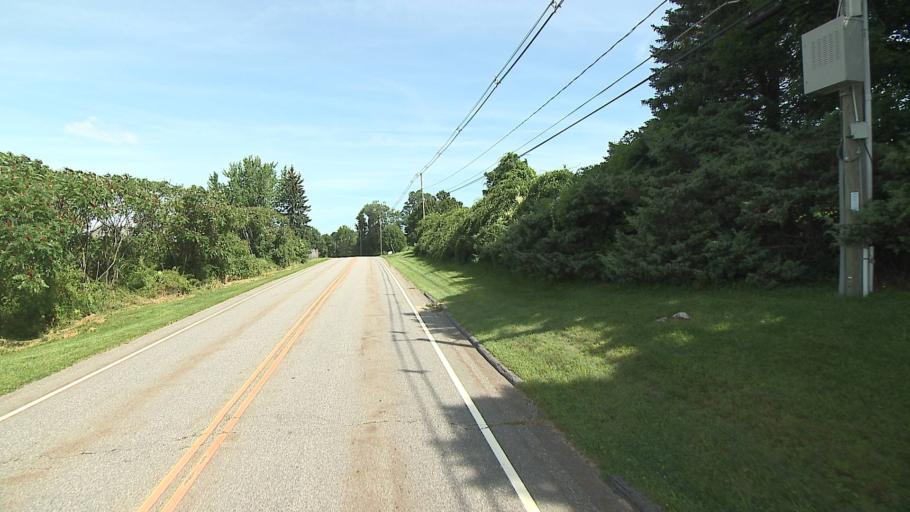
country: US
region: Connecticut
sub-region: Litchfield County
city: Bethlehem Village
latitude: 41.6739
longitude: -73.1970
